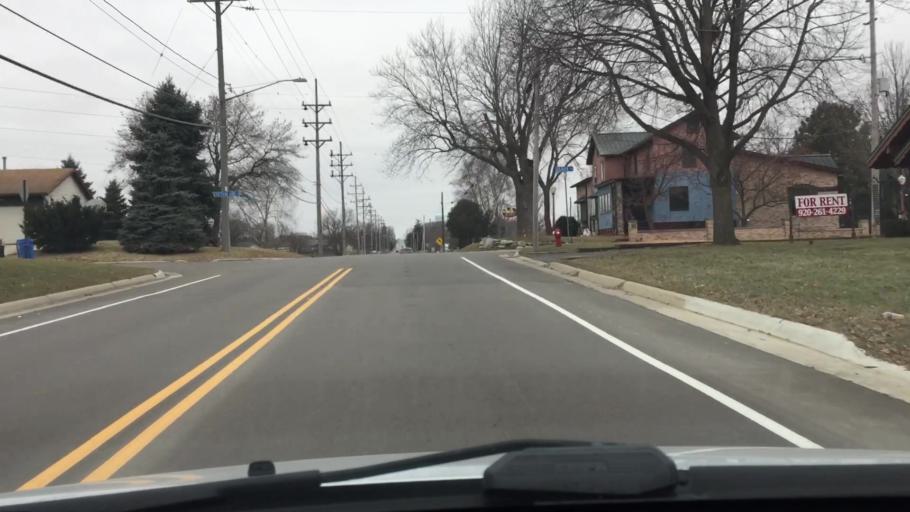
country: US
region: Wisconsin
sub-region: Jefferson County
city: Watertown
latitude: 43.1894
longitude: -88.7362
